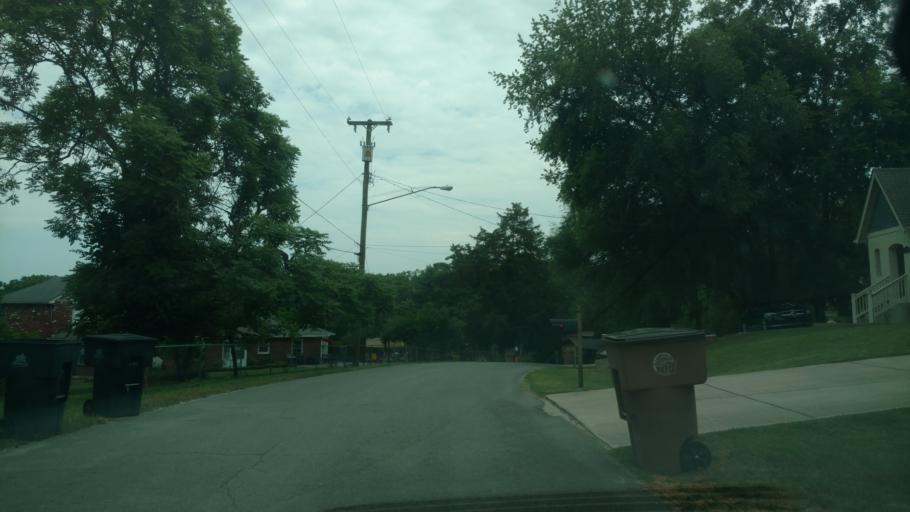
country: US
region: Tennessee
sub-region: Davidson County
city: Nashville
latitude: 36.1906
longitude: -86.7154
